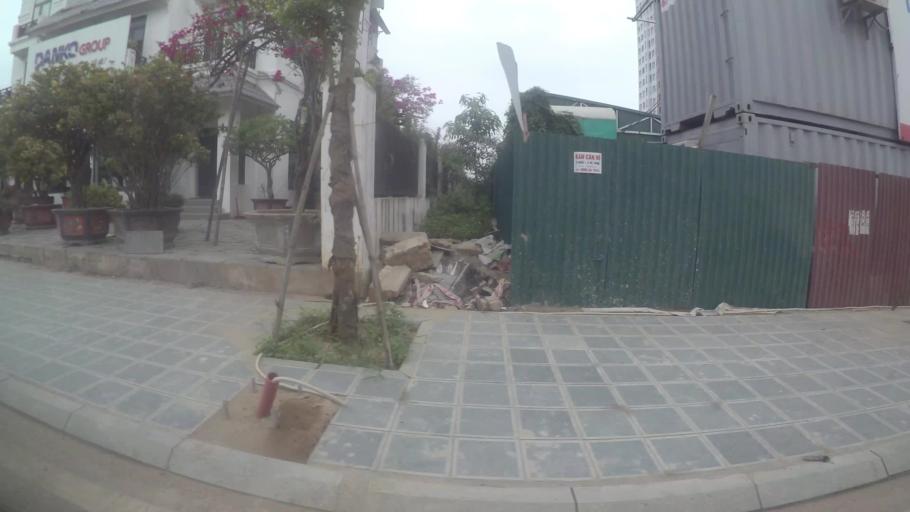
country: VN
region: Ha Noi
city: Ha Dong
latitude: 20.9826
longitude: 105.7420
